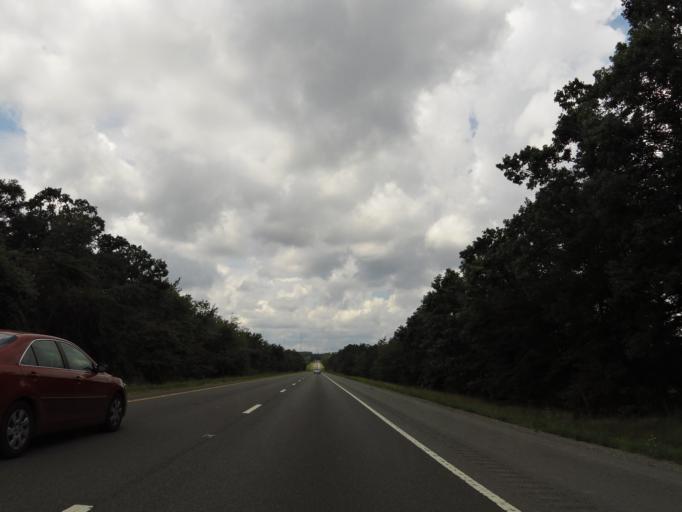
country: US
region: Tennessee
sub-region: Cumberland County
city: Crossville
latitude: 36.0369
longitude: -85.1031
